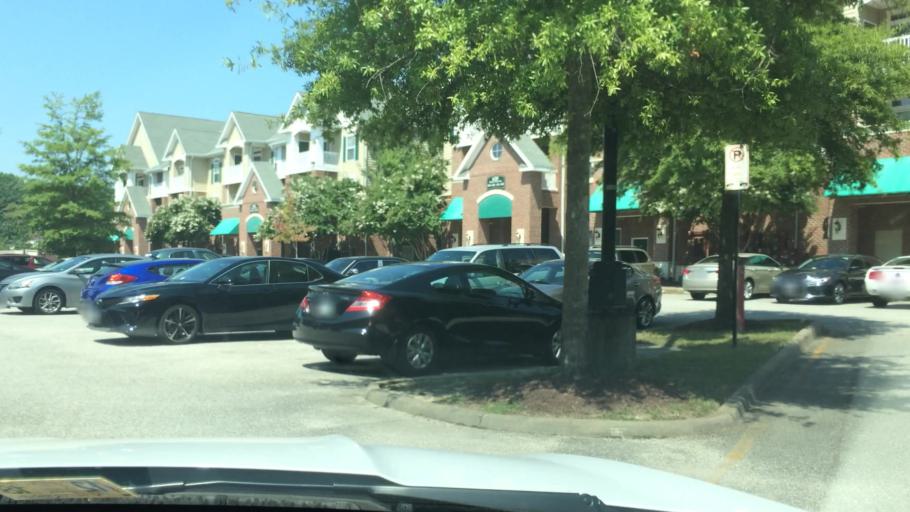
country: US
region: Virginia
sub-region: York County
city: Yorktown
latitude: 37.1418
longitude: -76.5199
